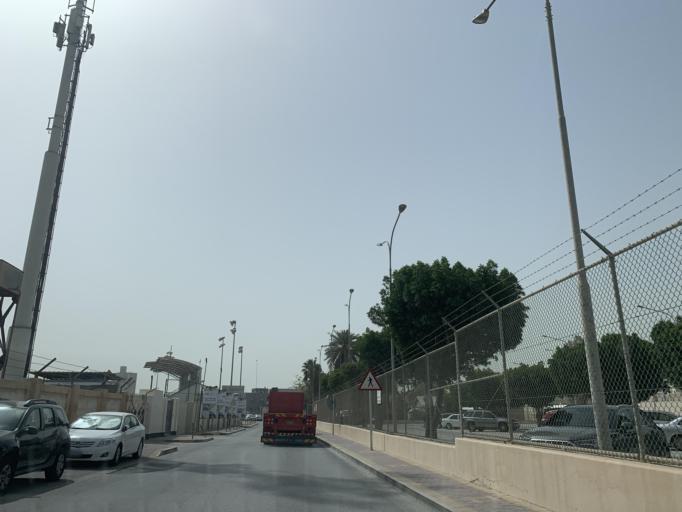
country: BH
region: Manama
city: Manama
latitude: 26.2085
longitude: 50.6054
